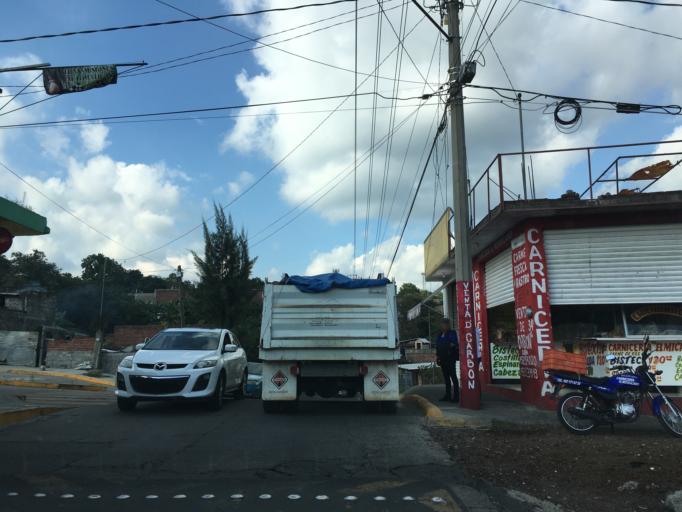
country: MX
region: Michoacan
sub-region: Uruapan
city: Uruapan
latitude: 19.4231
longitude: -102.0789
